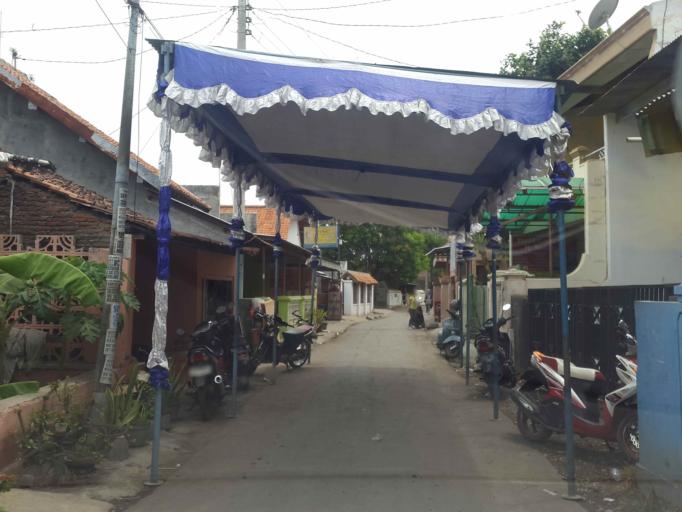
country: ID
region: Central Java
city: Tegal
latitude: -6.8878
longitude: 109.1366
